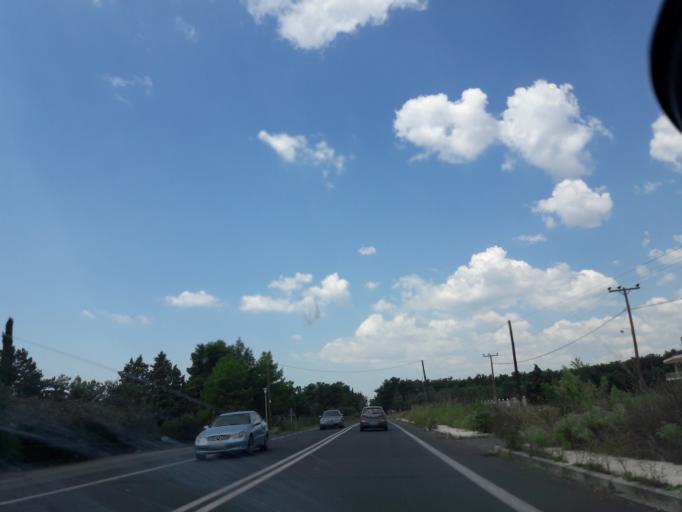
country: GR
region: Central Macedonia
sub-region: Nomos Thessalonikis
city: Souroti
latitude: 40.5109
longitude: 23.0807
